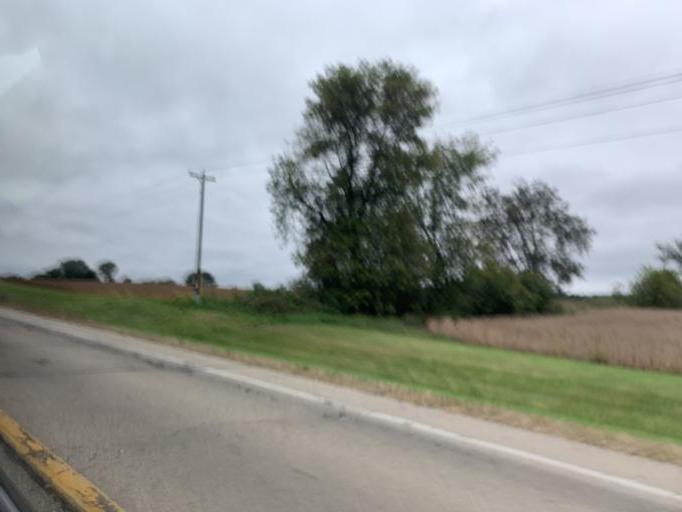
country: US
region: Wisconsin
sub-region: Grant County
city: Muscoda
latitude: 43.2198
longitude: -90.5333
